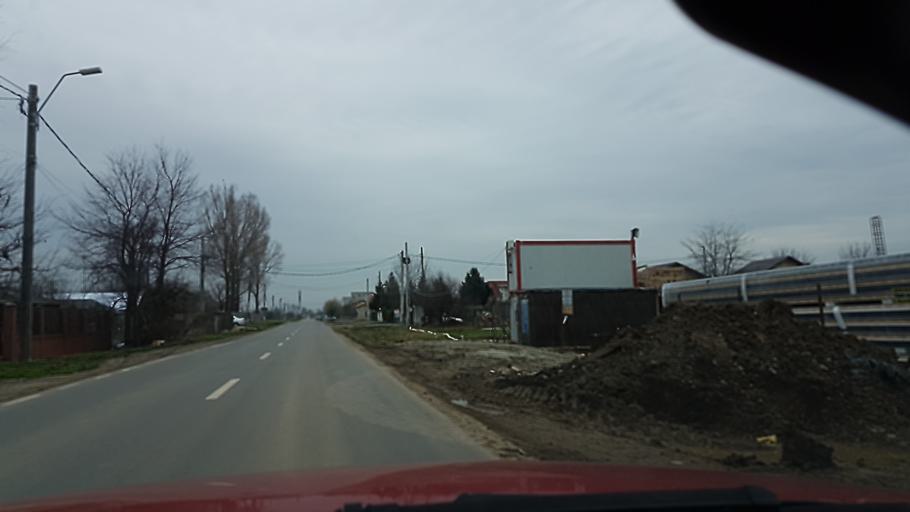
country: RO
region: Ilfov
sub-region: Comuna Tunari
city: Tunari
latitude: 44.5595
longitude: 26.1424
